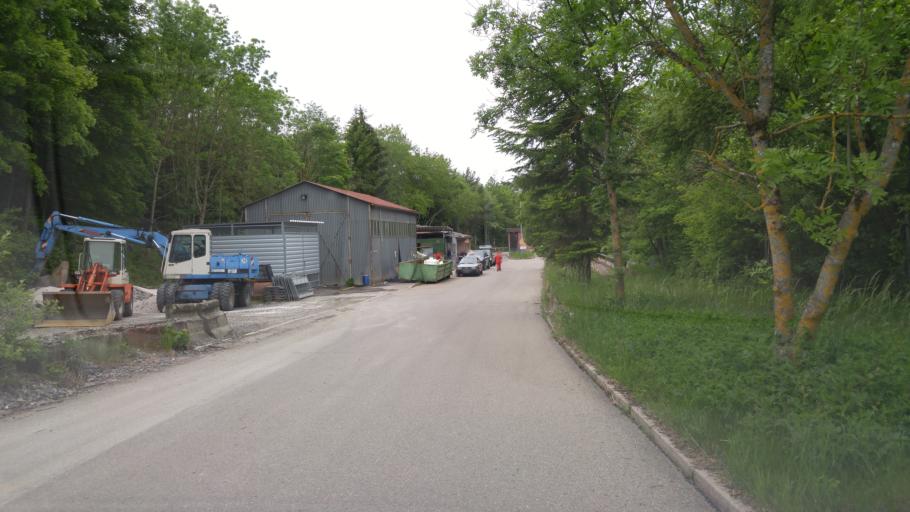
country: DE
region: Baden-Wuerttemberg
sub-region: Regierungsbezirk Stuttgart
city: Renningen
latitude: 48.7790
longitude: 8.9797
